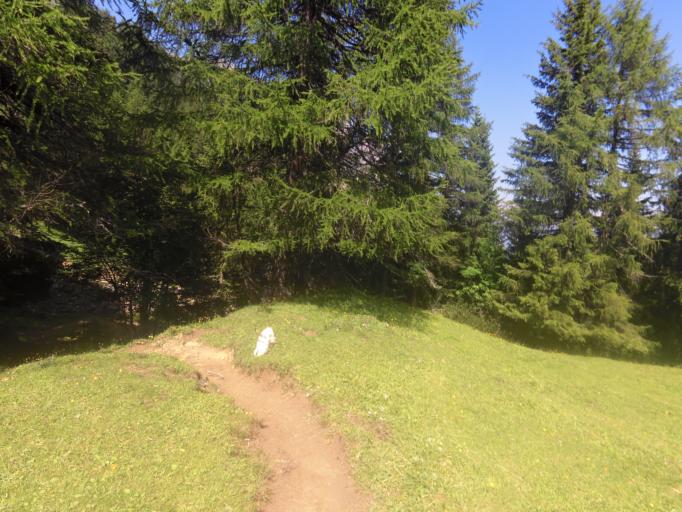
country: IT
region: Trentino-Alto Adige
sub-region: Bolzano
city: Siusi
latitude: 46.5130
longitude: 11.6049
